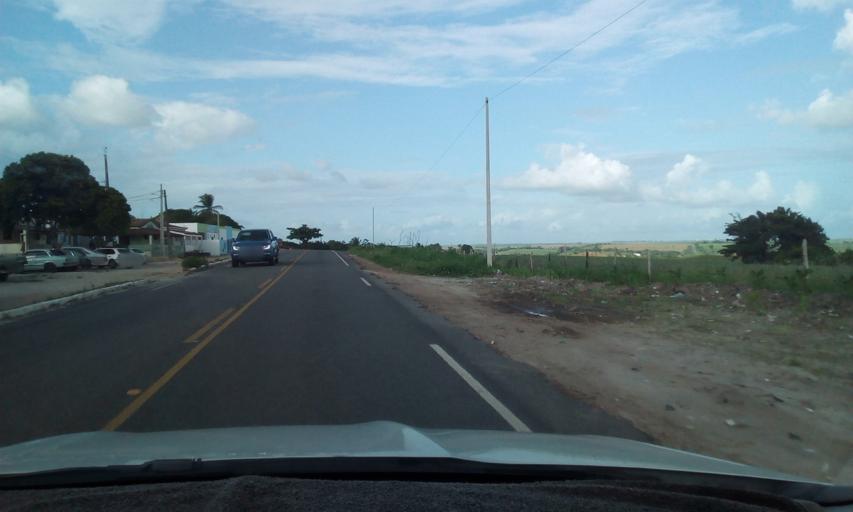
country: BR
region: Paraiba
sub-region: Mamanguape
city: Mamanguape
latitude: -6.8132
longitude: -35.2080
